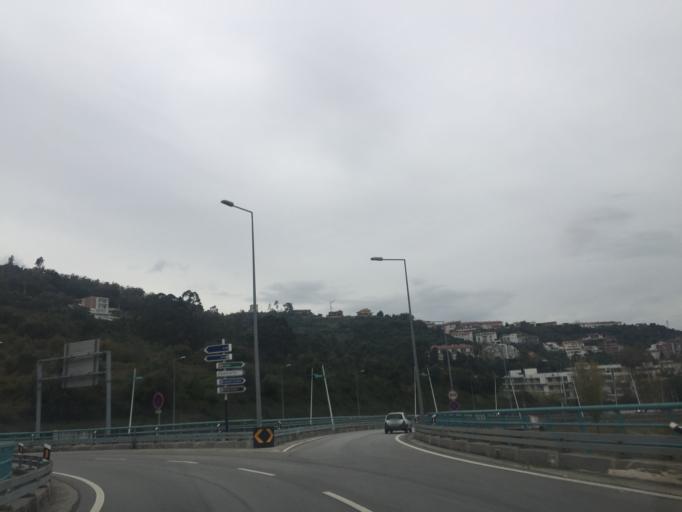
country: PT
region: Coimbra
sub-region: Coimbra
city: Coimbra
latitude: 40.1918
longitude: -8.4308
